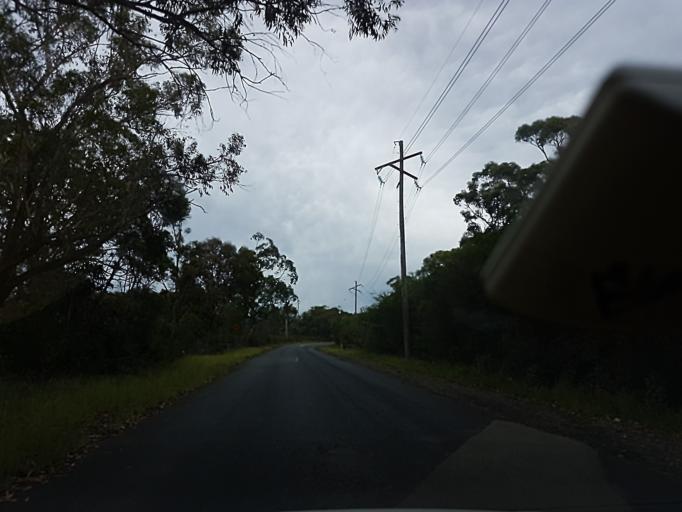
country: AU
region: New South Wales
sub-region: Warringah
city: Davidson
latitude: -33.7251
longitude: 151.2300
